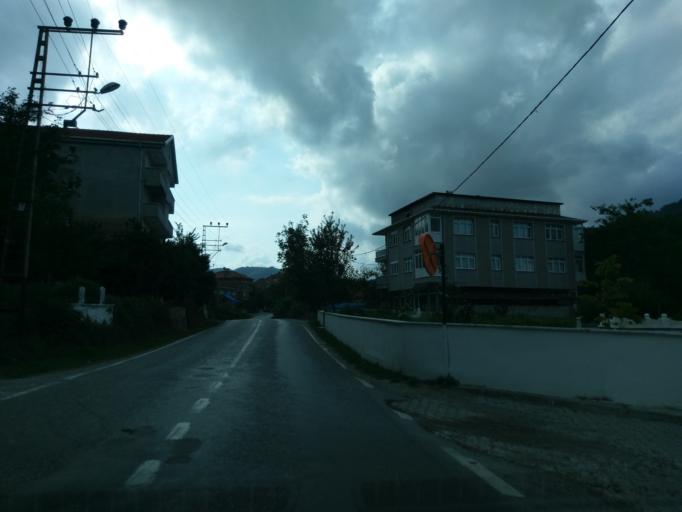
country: TR
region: Sinop
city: Helaldi
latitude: 41.9425
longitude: 34.3998
